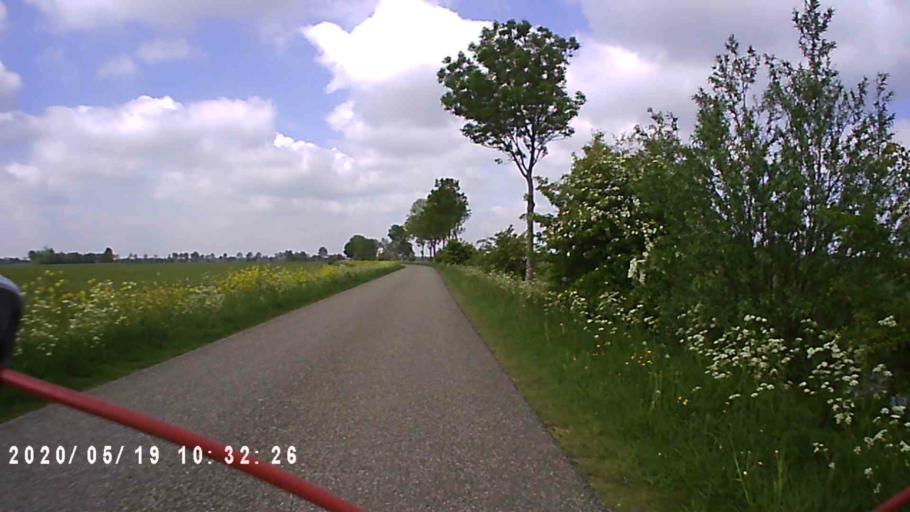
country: NL
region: Friesland
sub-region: Gemeente Kollumerland en Nieuwkruisland
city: Kollum
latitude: 53.2885
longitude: 6.1947
